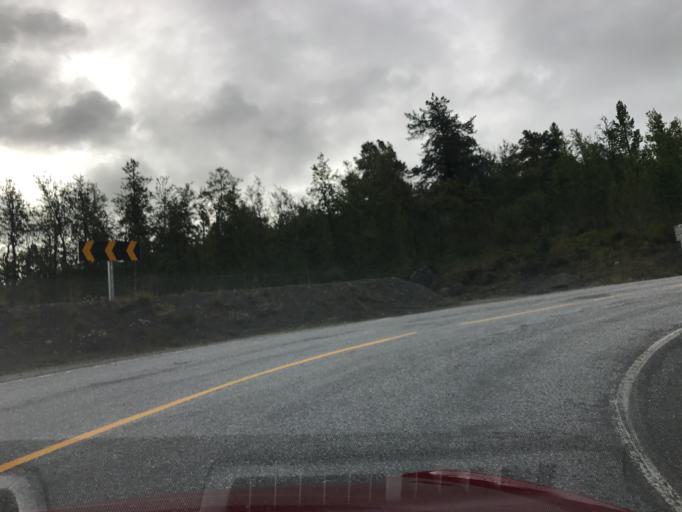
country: NO
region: Buskerud
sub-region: Hol
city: Hol
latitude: 60.4412
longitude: 8.4063
